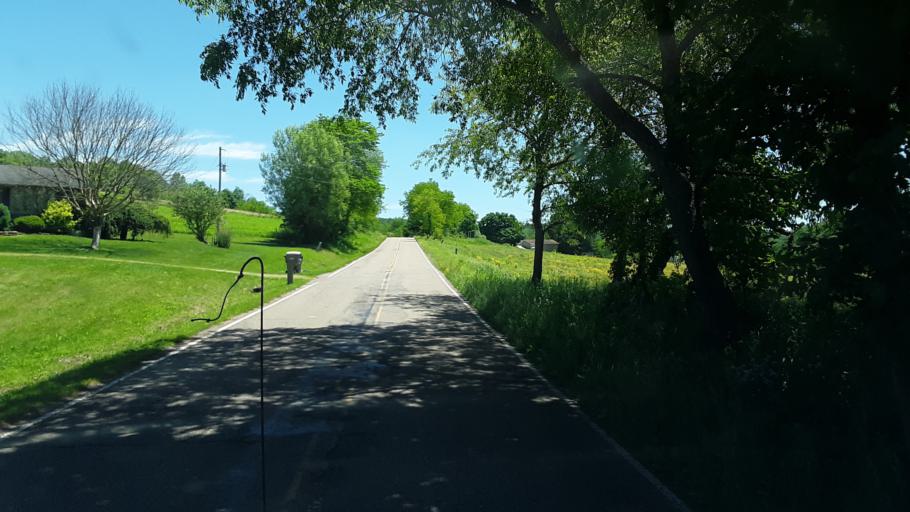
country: US
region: Ohio
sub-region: Coshocton County
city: Coshocton
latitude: 40.2844
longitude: -81.9907
